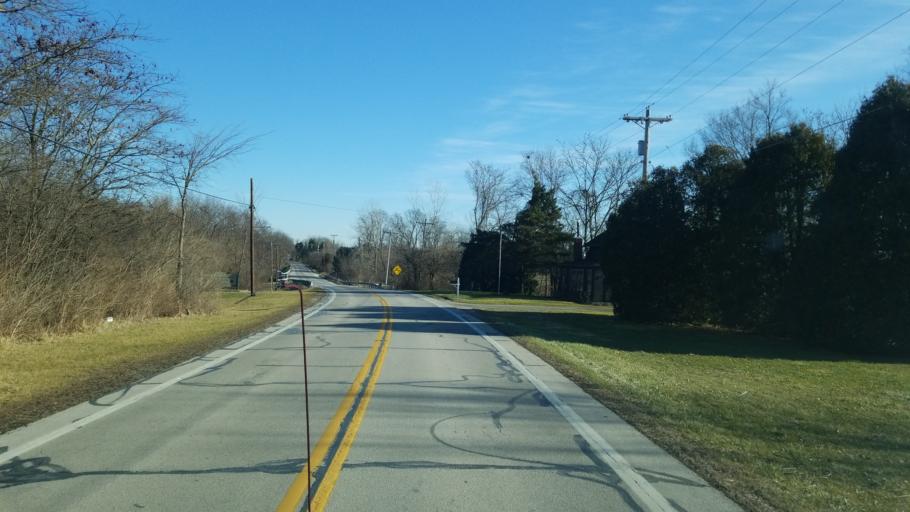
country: US
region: Ohio
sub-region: Wood County
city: Weston
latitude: 41.4095
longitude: -83.8797
